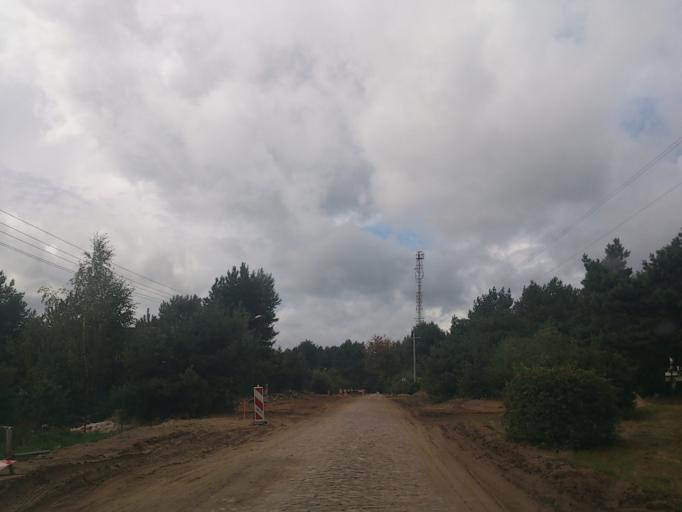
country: PL
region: Greater Poland Voivodeship
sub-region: Powiat poznanski
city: Kobylnica
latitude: 52.5166
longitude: 17.1355
